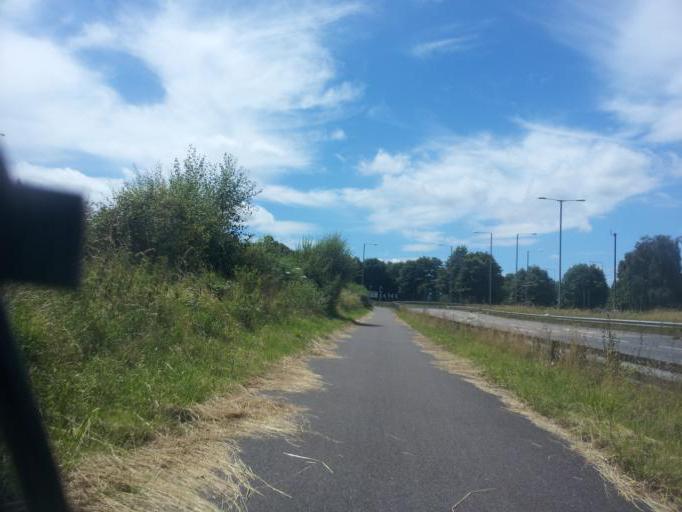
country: GB
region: England
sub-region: Kent
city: Kings Hill
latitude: 51.2823
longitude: 0.4045
